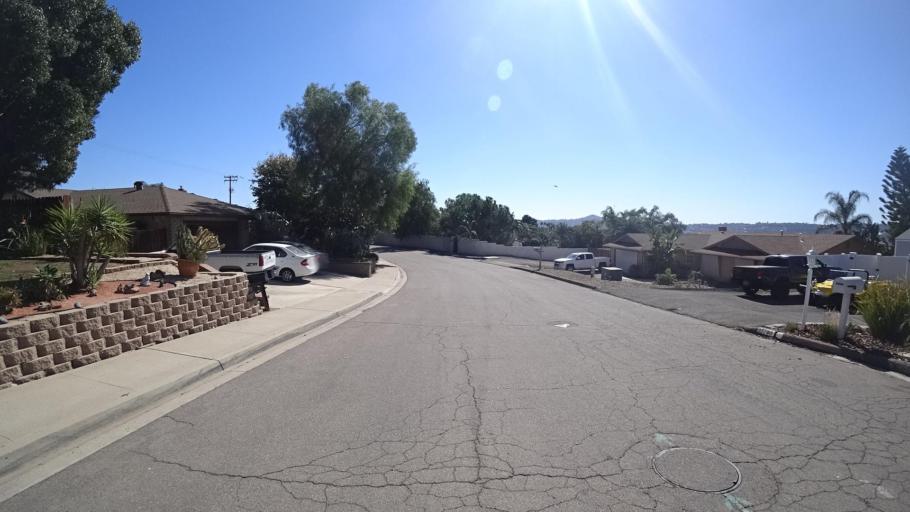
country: US
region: California
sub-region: San Diego County
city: Winter Gardens
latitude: 32.8286
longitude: -116.9523
